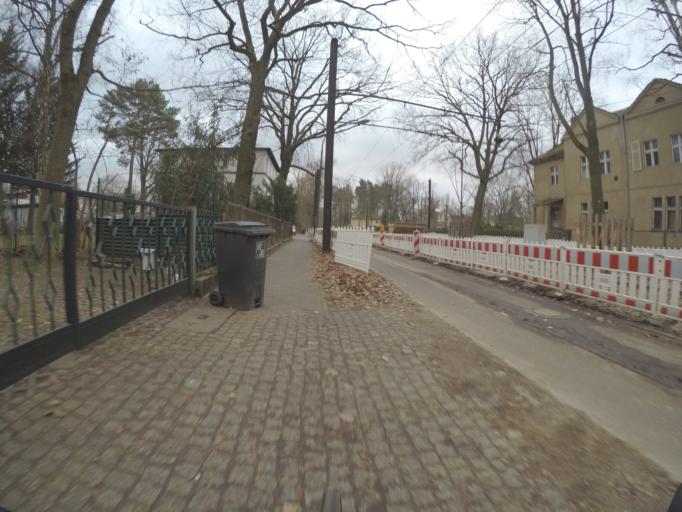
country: DE
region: Berlin
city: Grunau
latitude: 52.4178
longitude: 13.5893
